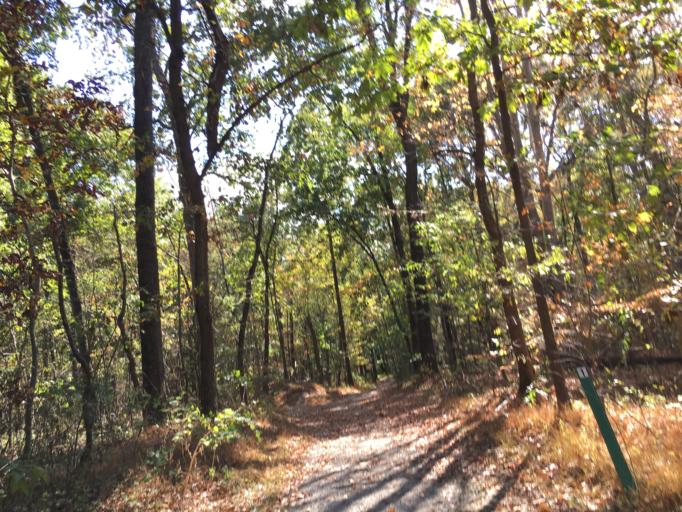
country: US
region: Pennsylvania
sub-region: York County
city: Yorklyn
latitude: 40.0136
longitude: -76.6420
